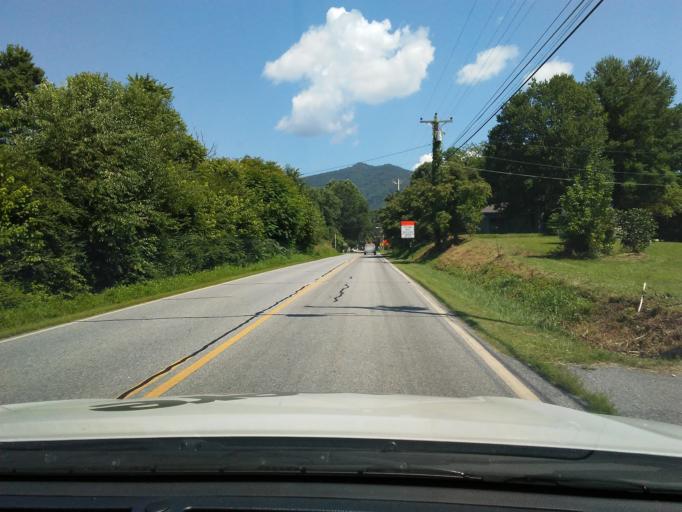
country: US
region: Georgia
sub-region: Towns County
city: Hiawassee
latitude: 34.9362
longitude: -83.8517
